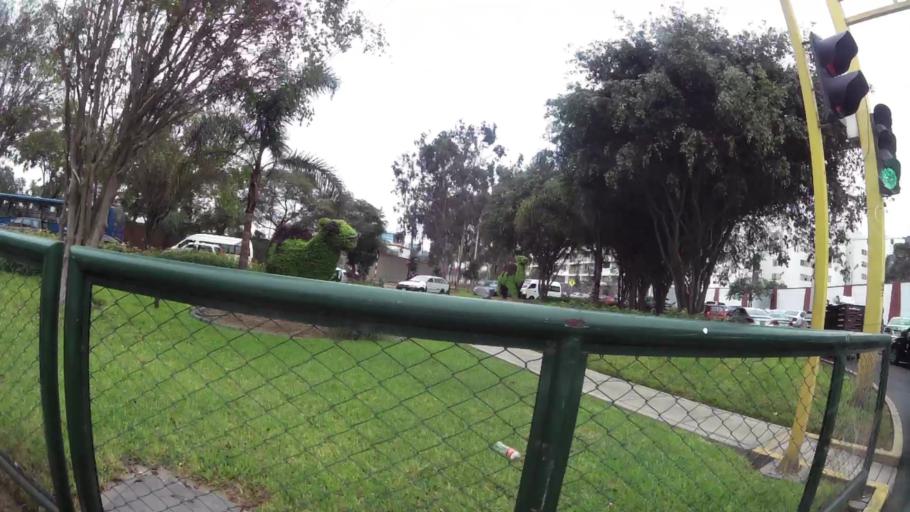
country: PE
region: Lima
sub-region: Lima
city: La Molina
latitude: -12.1030
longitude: -76.9627
